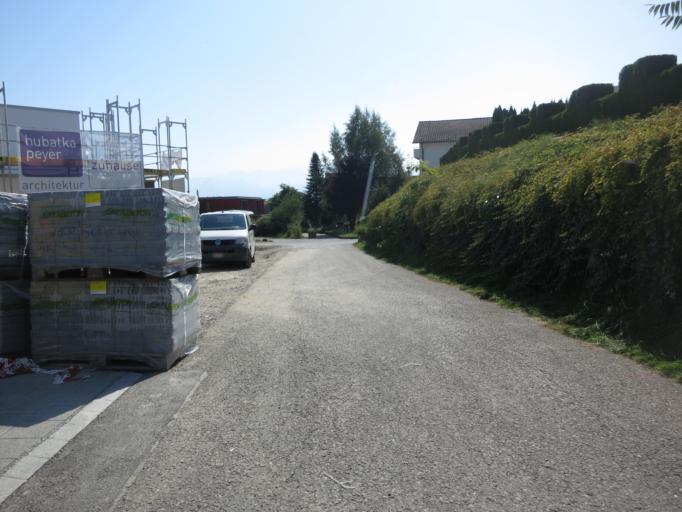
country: CH
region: Zurich
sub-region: Bezirk Meilen
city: Hombrechtikon
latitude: 47.2557
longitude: 8.7698
